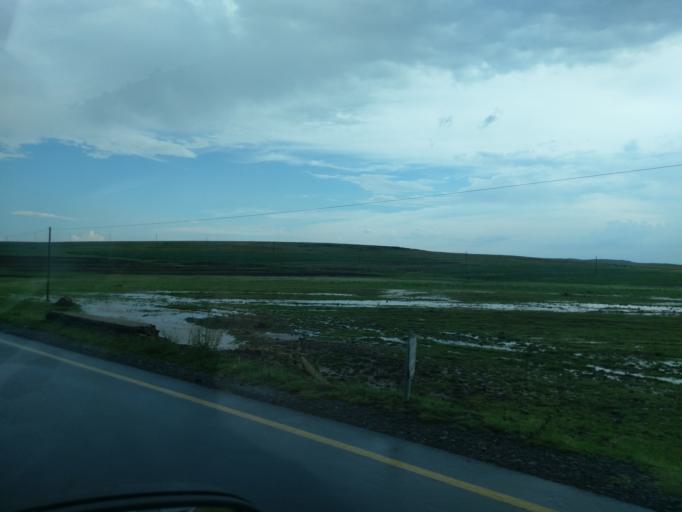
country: LS
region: Mafeteng
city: Mafeteng
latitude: -29.7867
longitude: 27.2046
